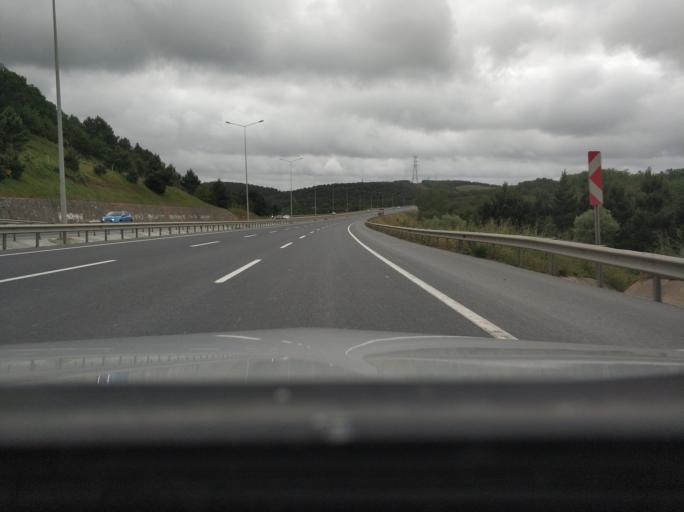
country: TR
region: Istanbul
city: Kemerburgaz
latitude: 41.1408
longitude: 28.9107
